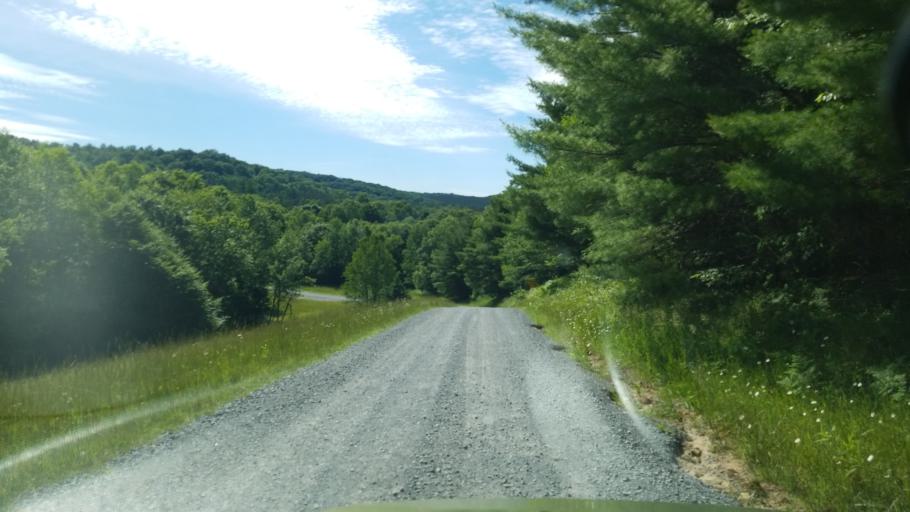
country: US
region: Pennsylvania
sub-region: Clearfield County
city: Clearfield
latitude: 41.2120
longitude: -78.4998
